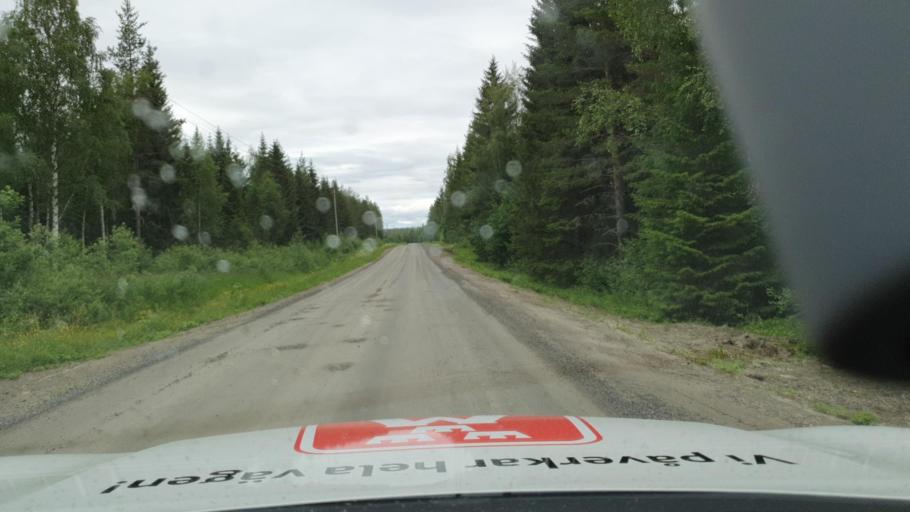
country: SE
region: Vaesterbotten
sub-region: Nordmalings Kommun
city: Nordmaling
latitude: 63.6538
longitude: 19.4392
